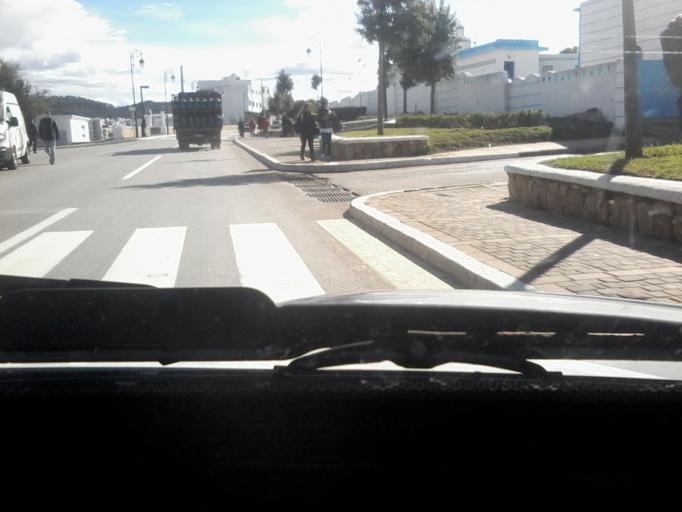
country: MA
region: Tanger-Tetouan
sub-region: Tetouan
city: Martil
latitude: 35.6914
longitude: -5.3311
